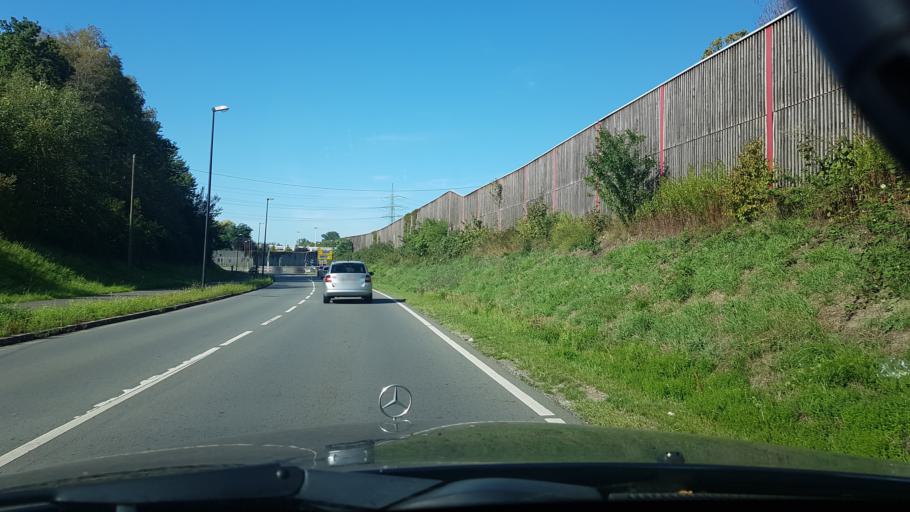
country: DE
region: North Rhine-Westphalia
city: Castrop-Rauxel
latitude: 51.5818
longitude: 7.3144
